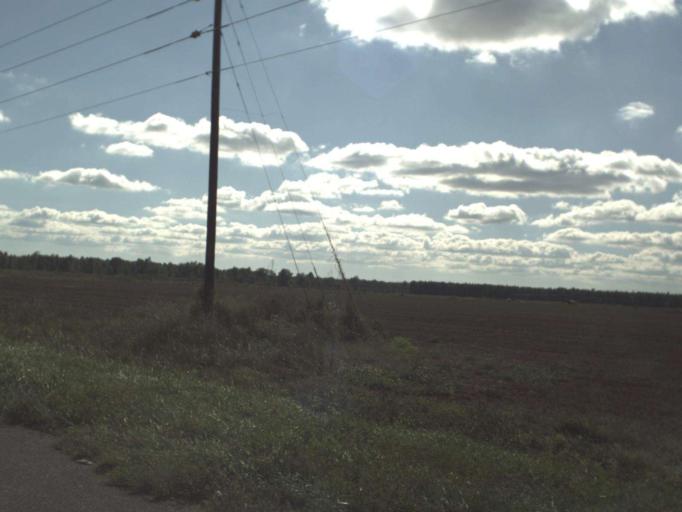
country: US
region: Florida
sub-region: Gulf County
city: Wewahitchka
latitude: 30.2103
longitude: -85.2087
